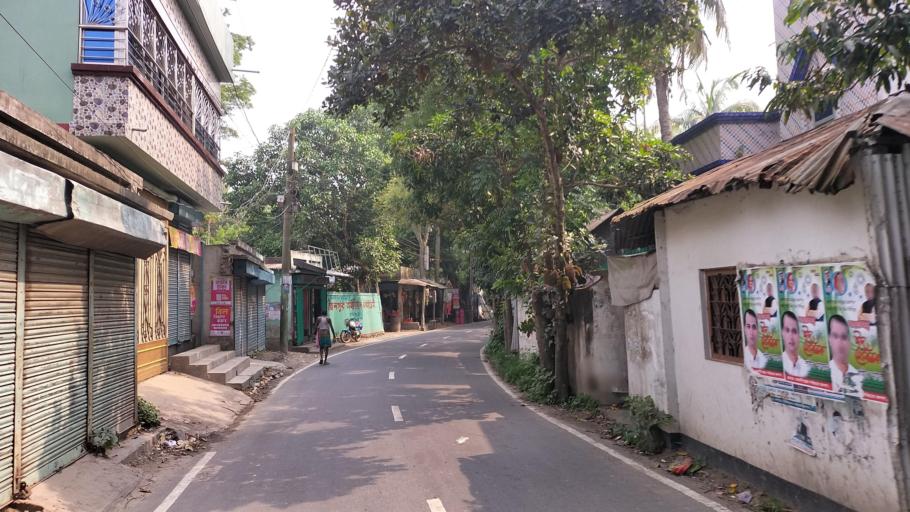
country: BD
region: Dhaka
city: Azimpur
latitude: 23.6985
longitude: 90.2943
